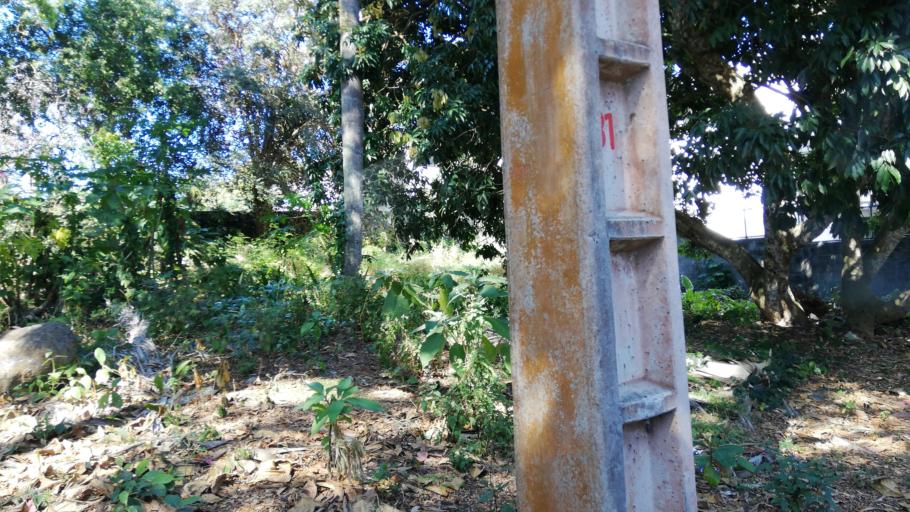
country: MU
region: Plaines Wilhems
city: Ebene
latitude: -20.2320
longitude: 57.4763
